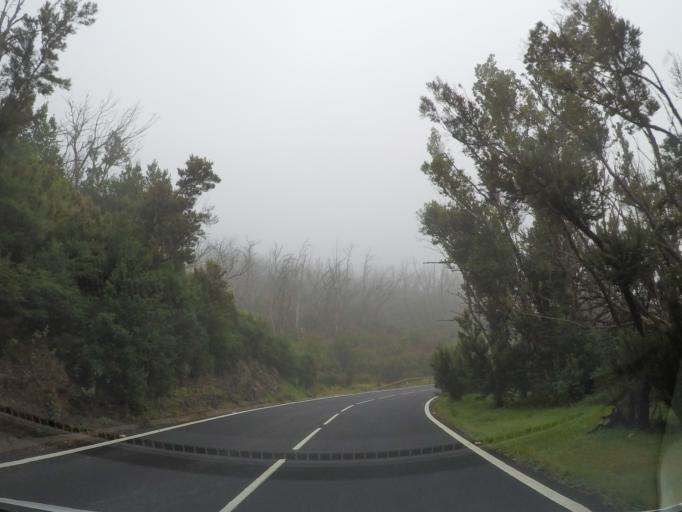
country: ES
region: Canary Islands
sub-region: Provincia de Santa Cruz de Tenerife
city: Vallehermosa
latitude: 28.1305
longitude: -17.2748
